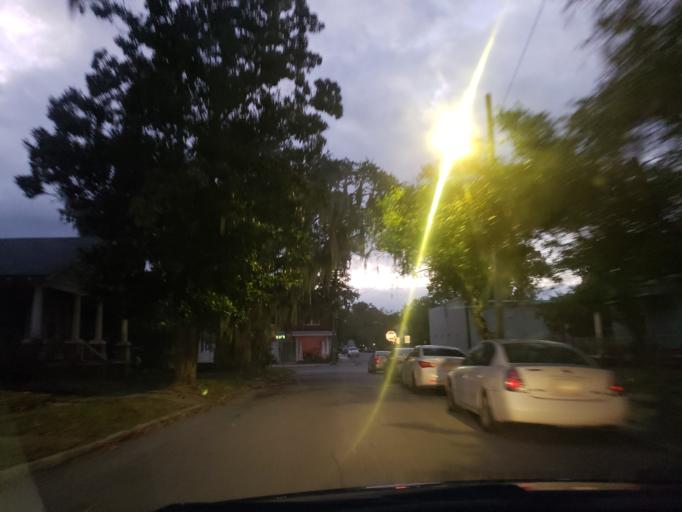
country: US
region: Georgia
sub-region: Chatham County
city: Savannah
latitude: 32.0496
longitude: -81.0843
